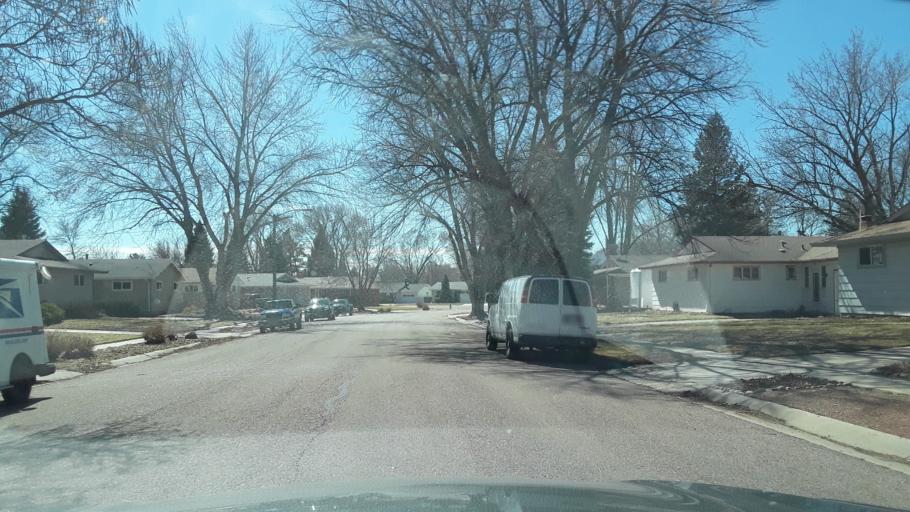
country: US
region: Colorado
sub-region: El Paso County
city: Colorado Springs
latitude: 38.8719
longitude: -104.8068
